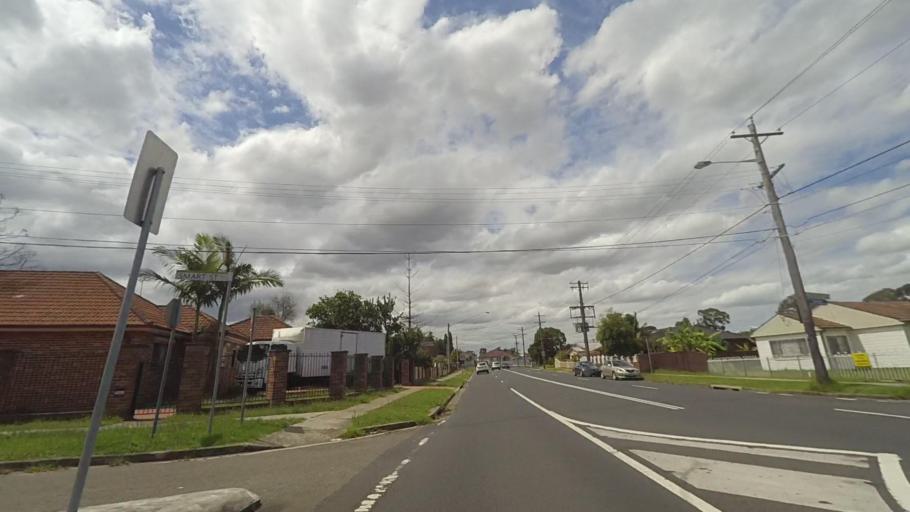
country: AU
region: New South Wales
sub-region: Fairfield
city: Fairfield Heights
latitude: -33.8647
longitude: 150.9505
